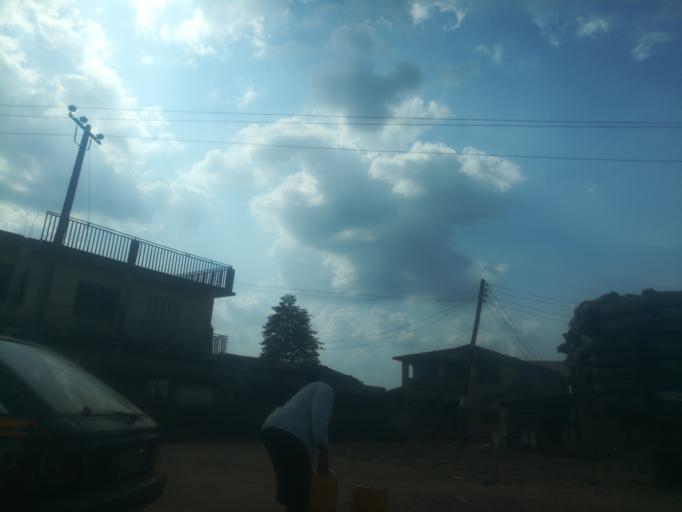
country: NG
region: Ogun
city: Abeokuta
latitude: 7.1730
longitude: 3.3388
